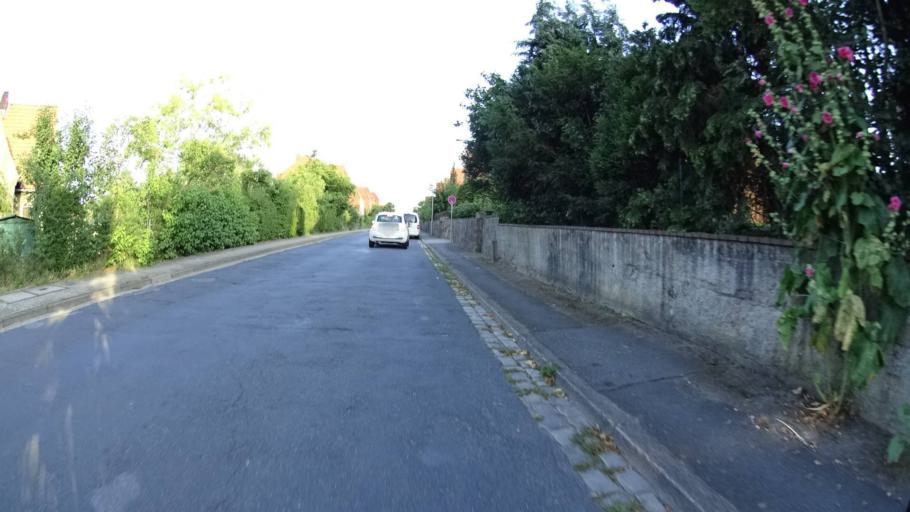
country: DE
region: Lower Saxony
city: Lueneburg
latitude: 53.2439
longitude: 10.3916
